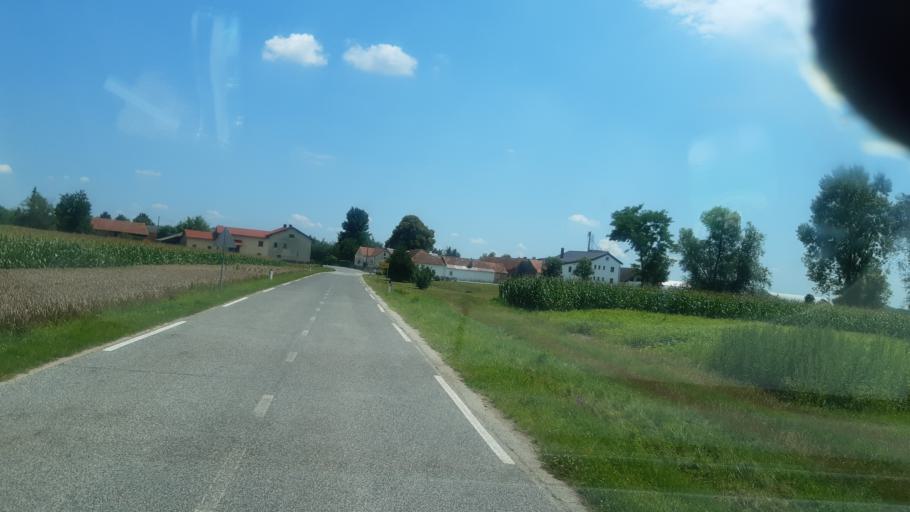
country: SI
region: Beltinci
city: Gancani
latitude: 46.6588
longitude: 16.2493
